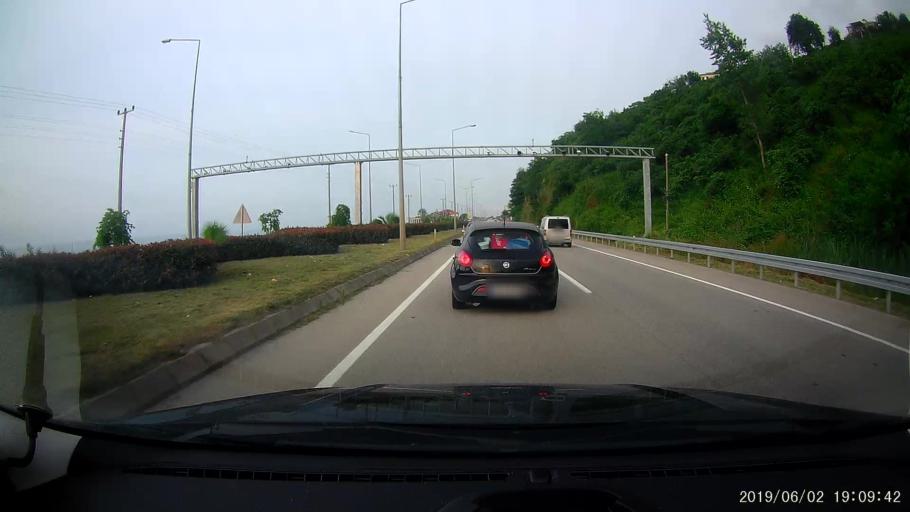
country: TR
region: Ordu
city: Gulyali
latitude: 40.9723
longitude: 38.0327
